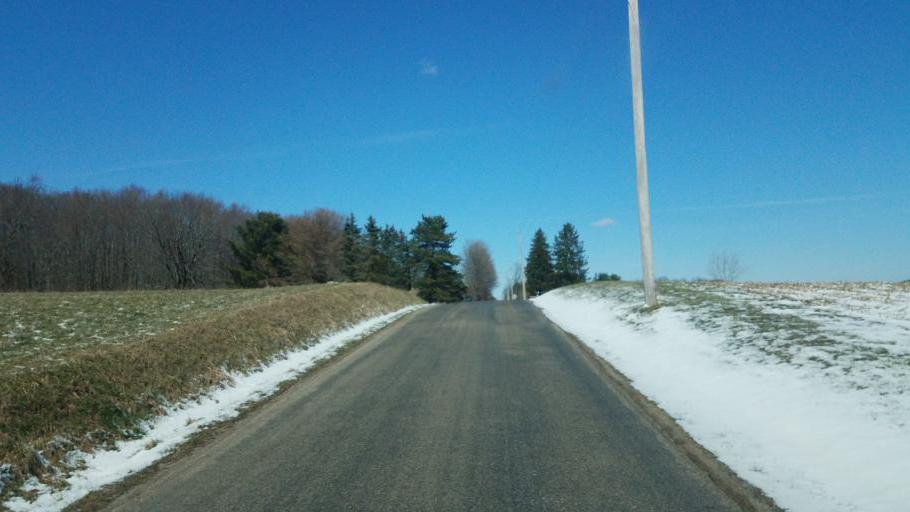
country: US
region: Ohio
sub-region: Richland County
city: Lexington
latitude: 40.6026
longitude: -82.6149
